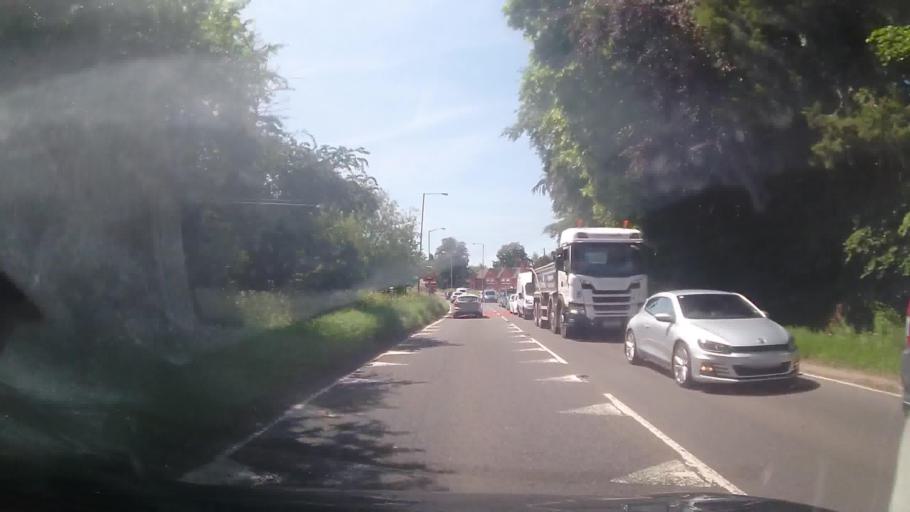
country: GB
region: England
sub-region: Herefordshire
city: Hereford
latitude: 52.0789
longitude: -2.7220
